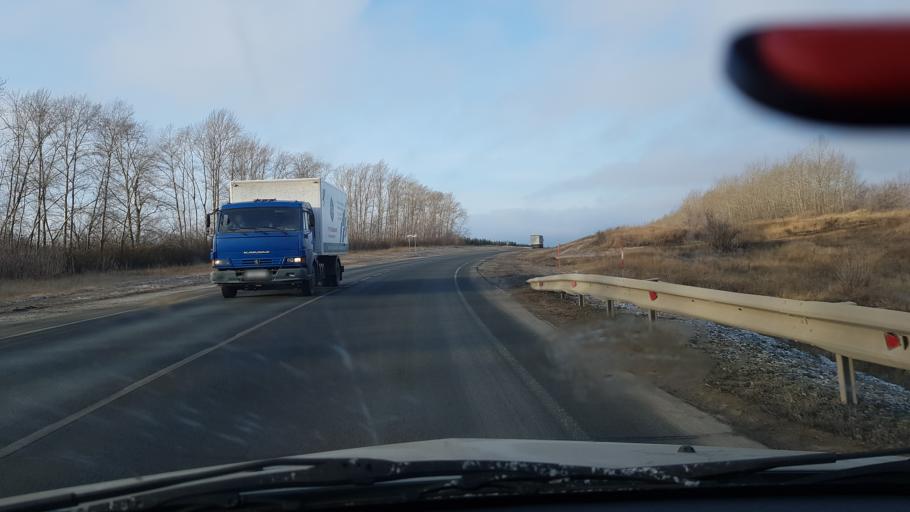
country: RU
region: Tatarstan
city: Laishevo
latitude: 55.3915
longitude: 49.7926
